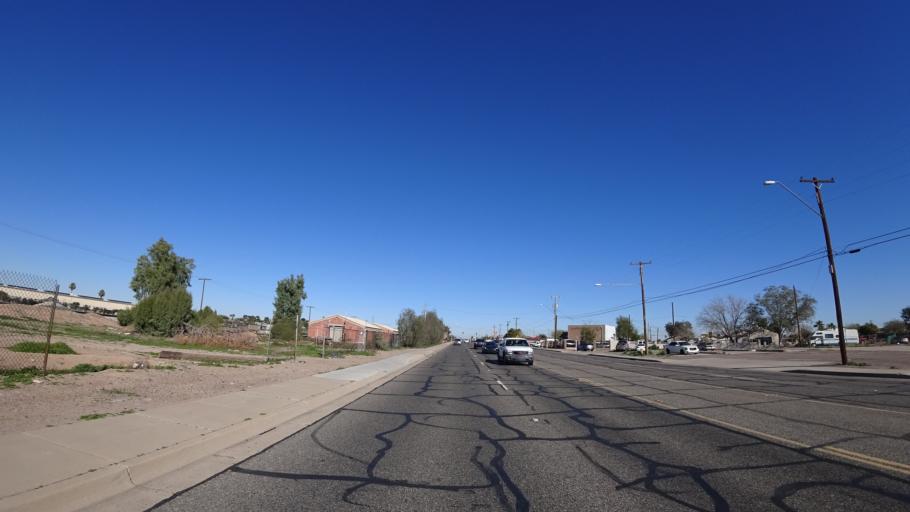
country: US
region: Arizona
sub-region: Maricopa County
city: Avondale
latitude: 33.4280
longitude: -112.3518
